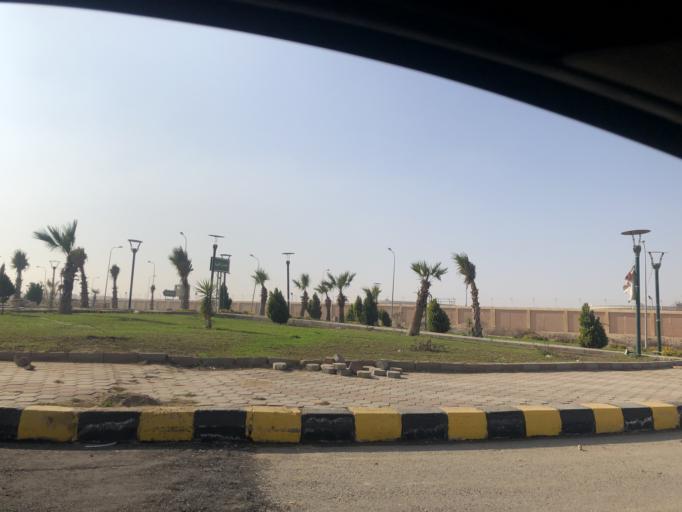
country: EG
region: Al Jizah
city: Madinat Sittah Uktubar
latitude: 29.9312
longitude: 31.0424
